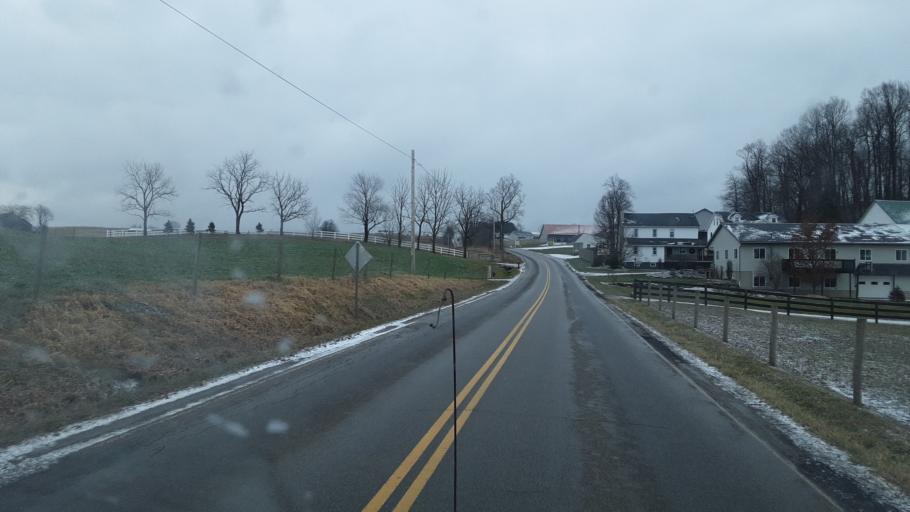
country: US
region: Ohio
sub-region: Tuscarawas County
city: Sugarcreek
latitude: 40.6182
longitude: -81.7304
